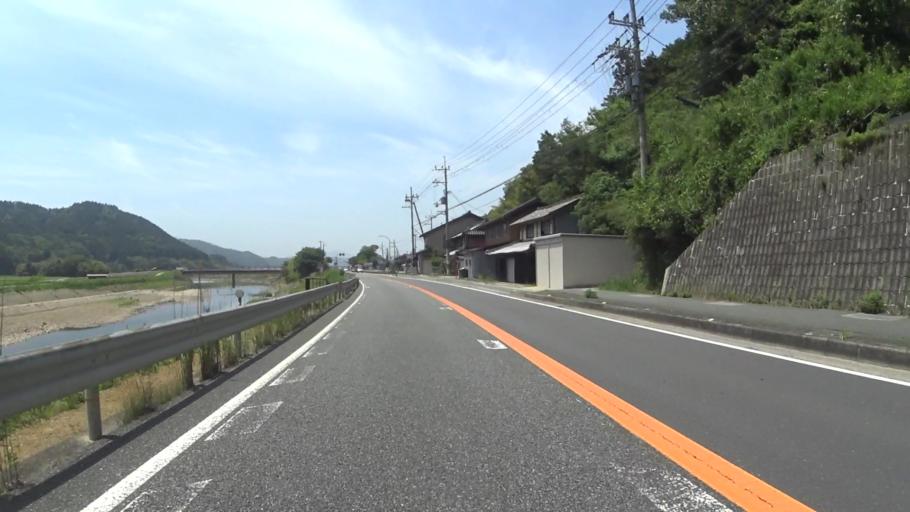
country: JP
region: Kyoto
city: Ayabe
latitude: 35.2552
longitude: 135.2035
